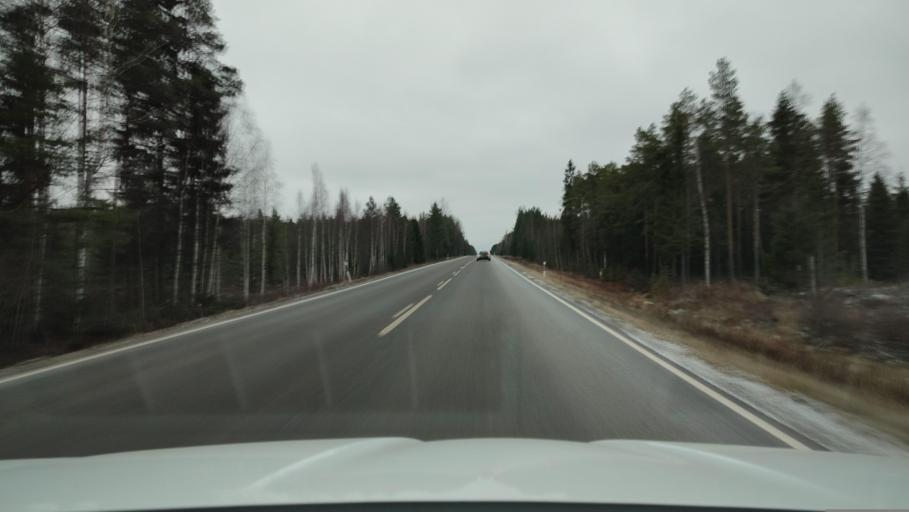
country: FI
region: Ostrobothnia
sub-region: Sydosterbotten
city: Naerpes
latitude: 62.5747
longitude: 21.4896
